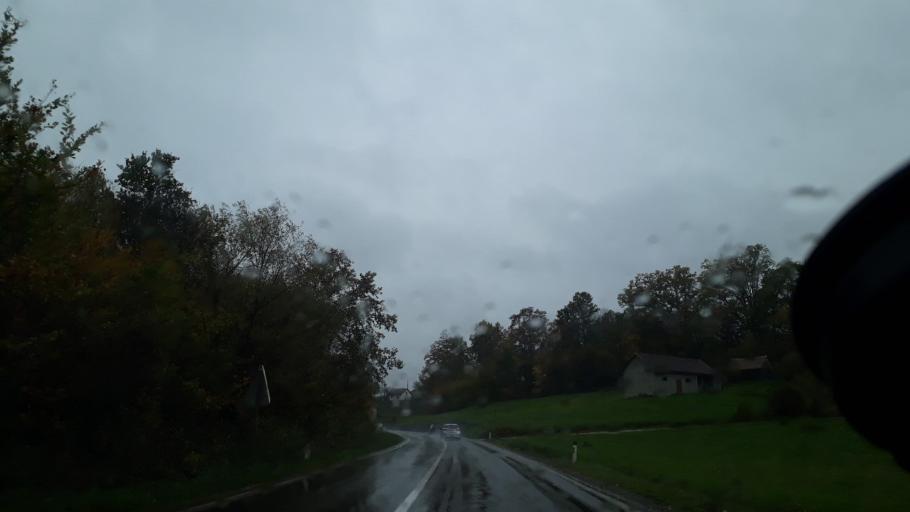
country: BA
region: Republika Srpska
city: Maglajani
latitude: 44.8665
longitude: 17.4657
